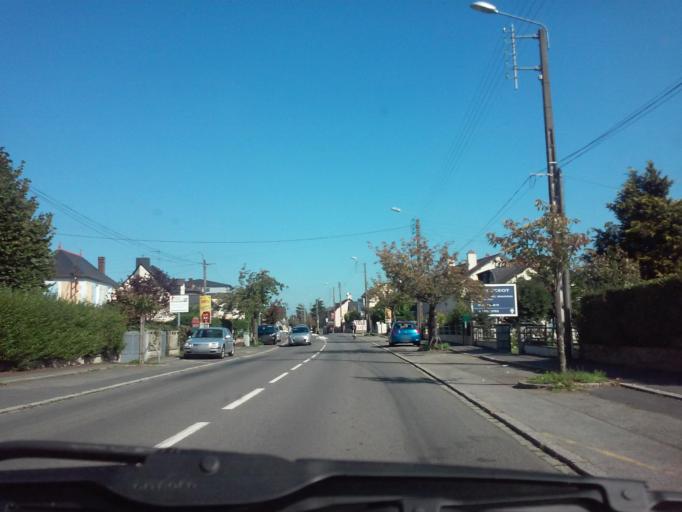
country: FR
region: Brittany
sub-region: Departement d'Ille-et-Vilaine
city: Betton
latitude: 48.1750
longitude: -1.6399
